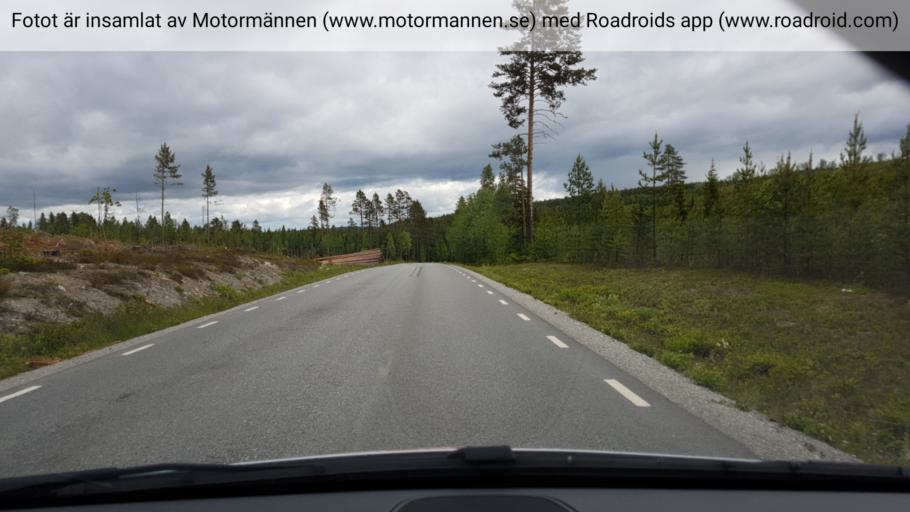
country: SE
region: Jaemtland
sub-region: Braecke Kommun
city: Braecke
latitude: 63.1239
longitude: 15.4939
